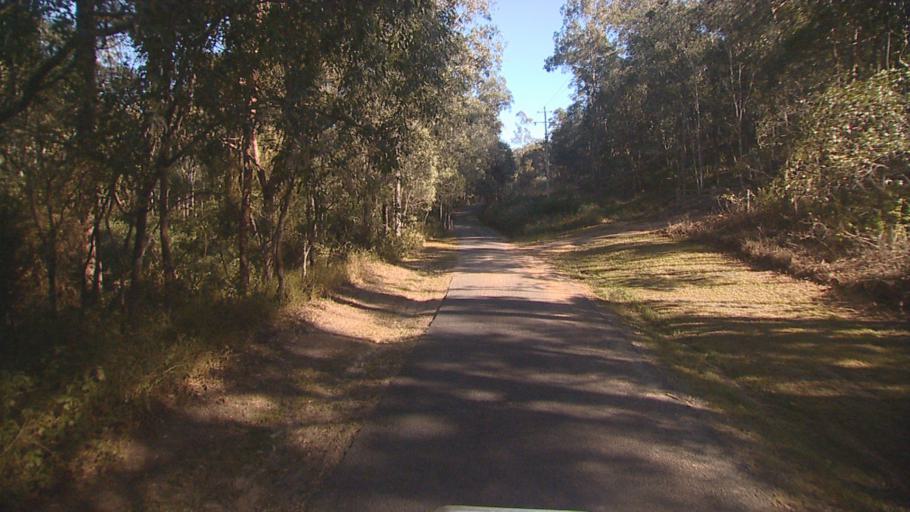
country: AU
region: Queensland
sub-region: Logan
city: Windaroo
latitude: -27.7937
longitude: 153.1720
